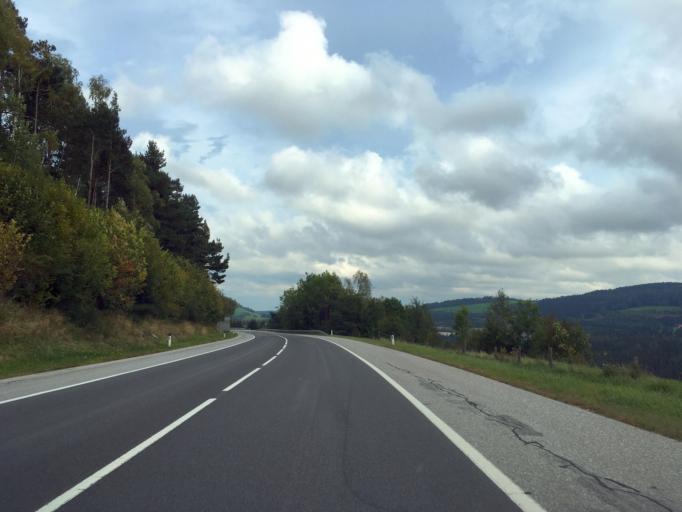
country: AT
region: Lower Austria
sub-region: Politischer Bezirk Neunkirchen
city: Monichkirchen
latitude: 47.5231
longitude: 16.0633
